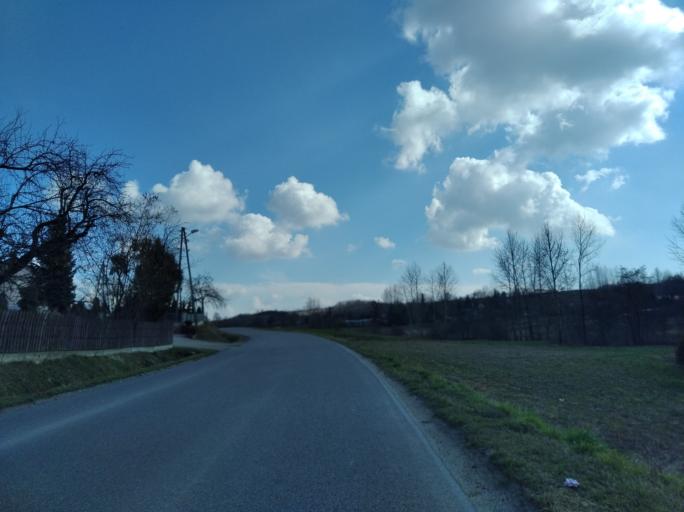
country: PL
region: Subcarpathian Voivodeship
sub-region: Powiat debicki
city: Brzostek
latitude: 49.8609
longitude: 21.4692
